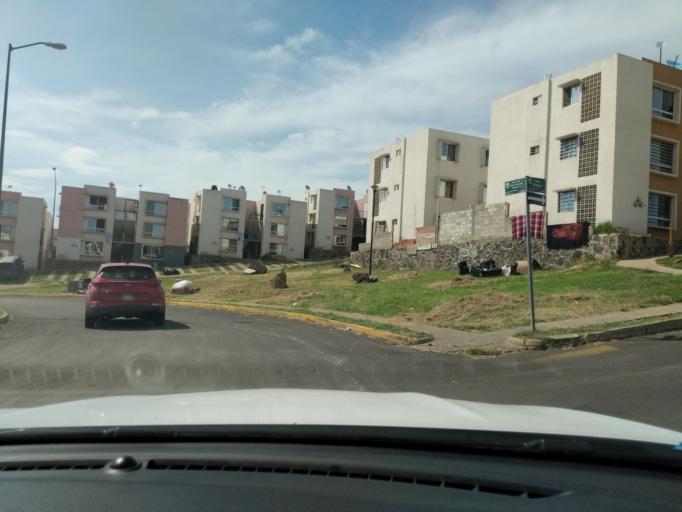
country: MX
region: Jalisco
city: San Jose del Castillo
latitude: 20.5224
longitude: -103.2249
